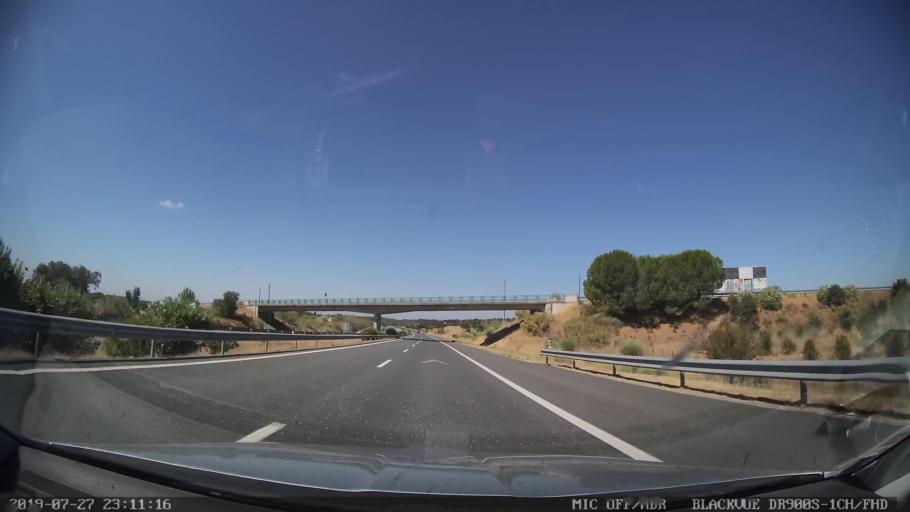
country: PT
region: Evora
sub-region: Estremoz
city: Estremoz
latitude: 38.7522
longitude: -7.7257
